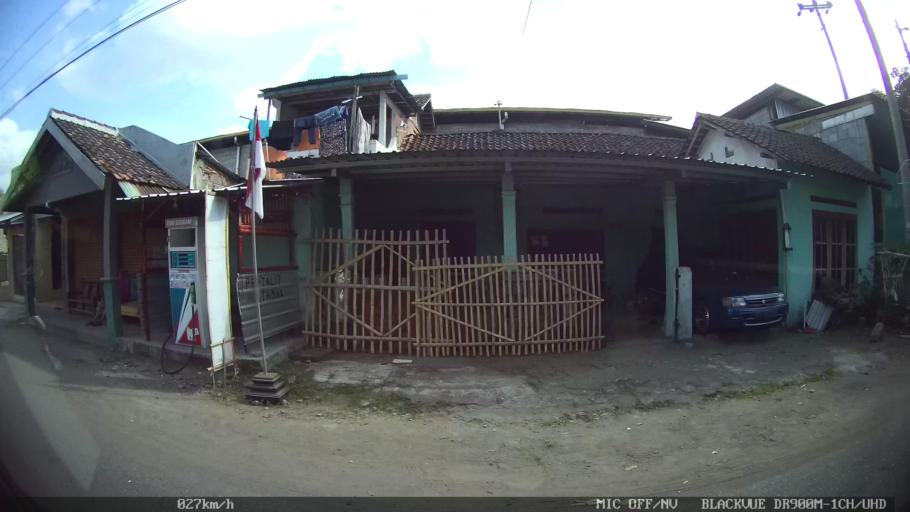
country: ID
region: Daerah Istimewa Yogyakarta
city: Kasihan
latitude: -7.8281
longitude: 110.3584
